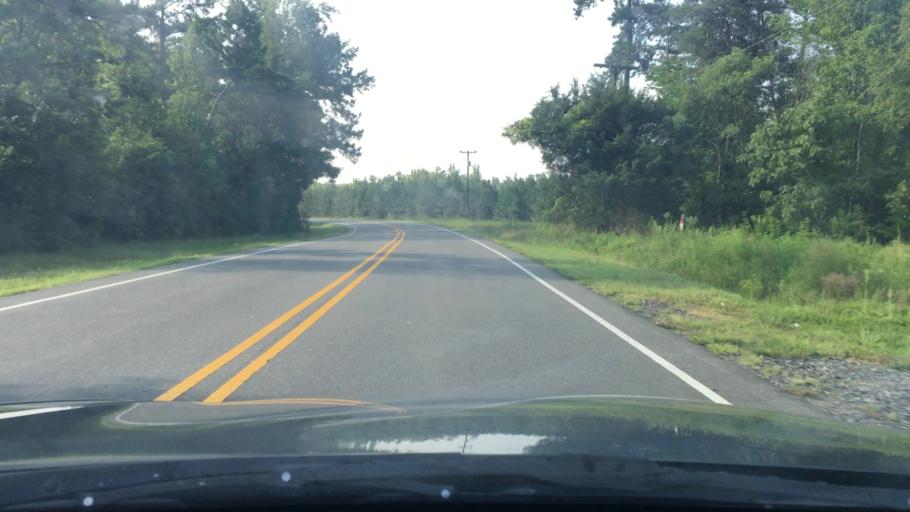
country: US
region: North Carolina
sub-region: Alamance County
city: Green Level
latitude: 36.2591
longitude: -79.3372
